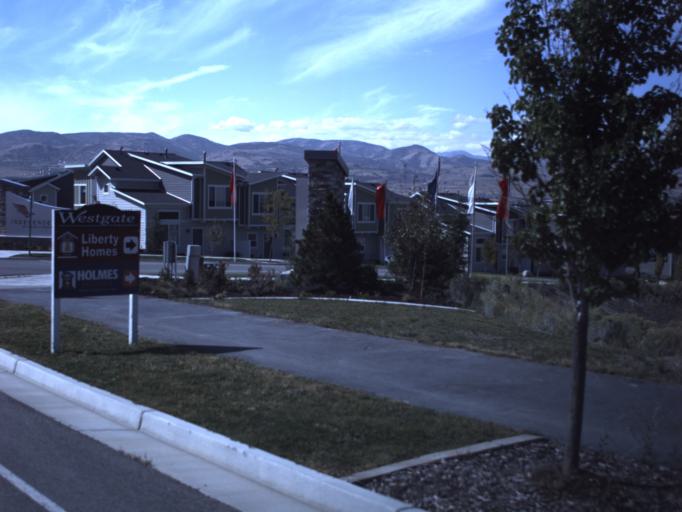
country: US
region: Utah
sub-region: Salt Lake County
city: Bluffdale
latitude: 40.4755
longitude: -111.9112
